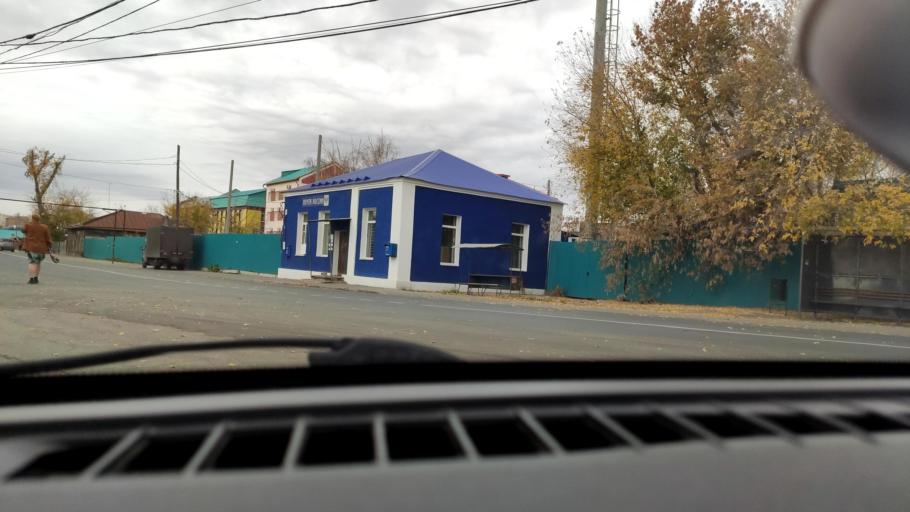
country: RU
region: Samara
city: Samara
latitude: 53.1828
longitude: 50.1299
